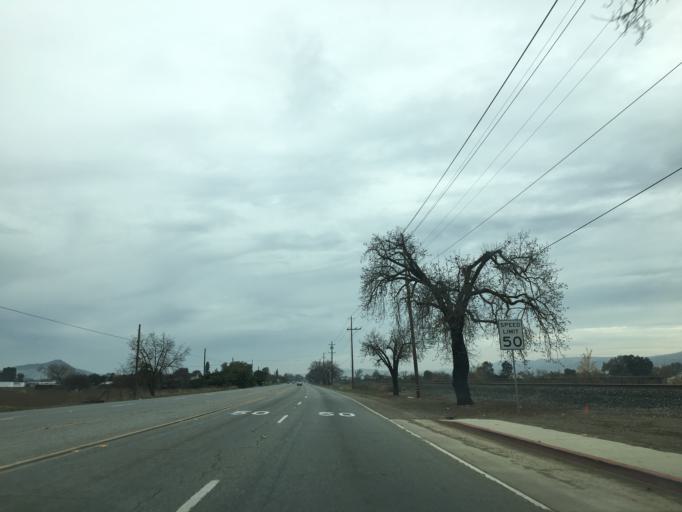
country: US
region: California
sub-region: Santa Clara County
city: San Martin
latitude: 37.0682
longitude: -121.6003
